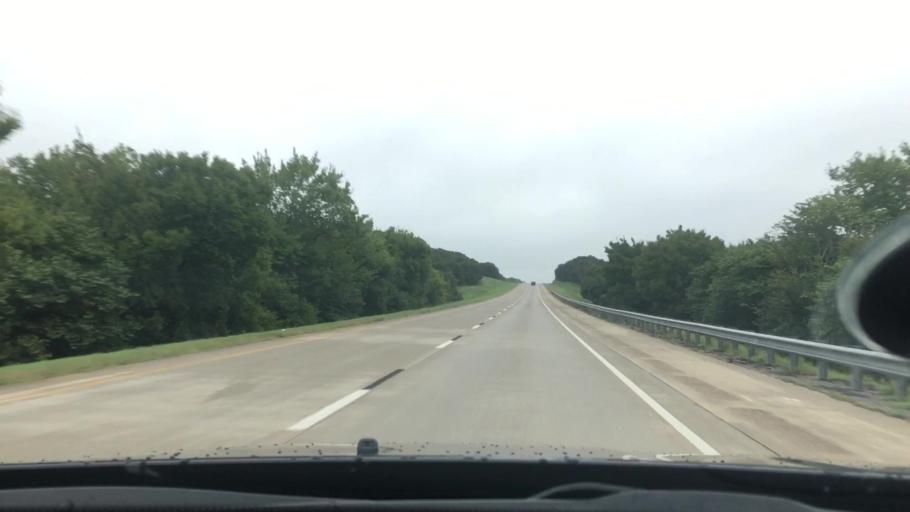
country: US
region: Oklahoma
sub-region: Okfuskee County
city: Boley
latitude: 35.3844
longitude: -96.5781
